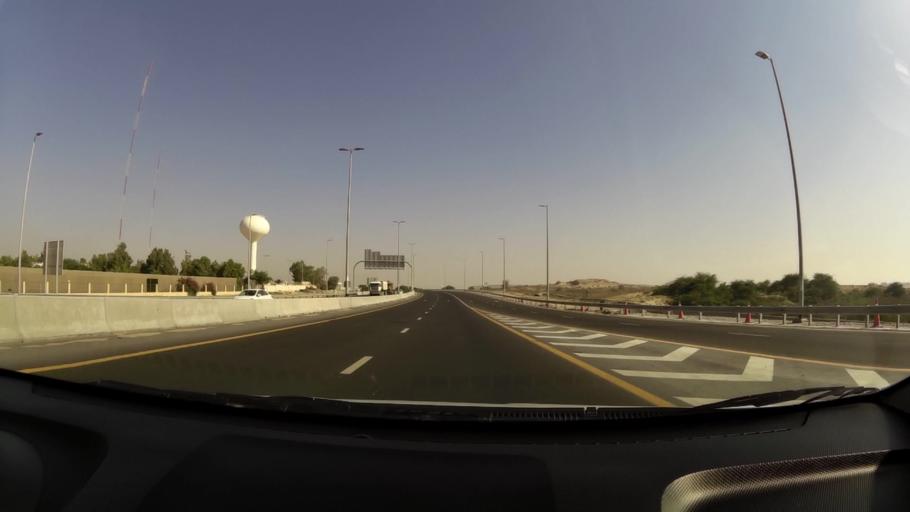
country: AE
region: Umm al Qaywayn
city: Umm al Qaywayn
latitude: 25.4899
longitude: 55.5525
